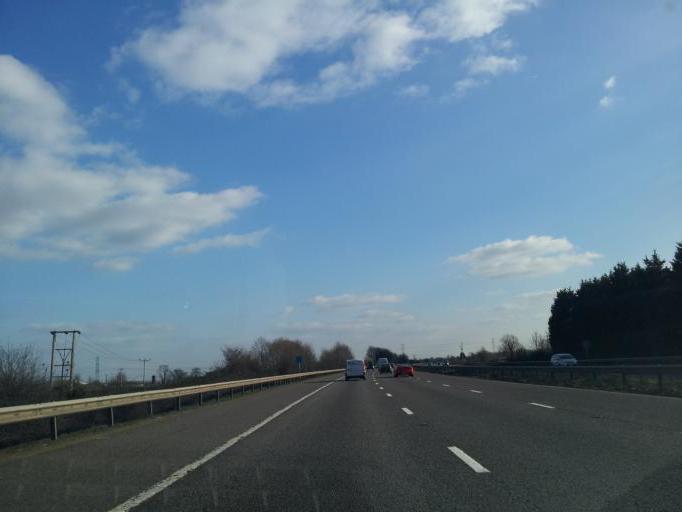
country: GB
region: England
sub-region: Somerset
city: Puriton
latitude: 51.1389
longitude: -2.9698
